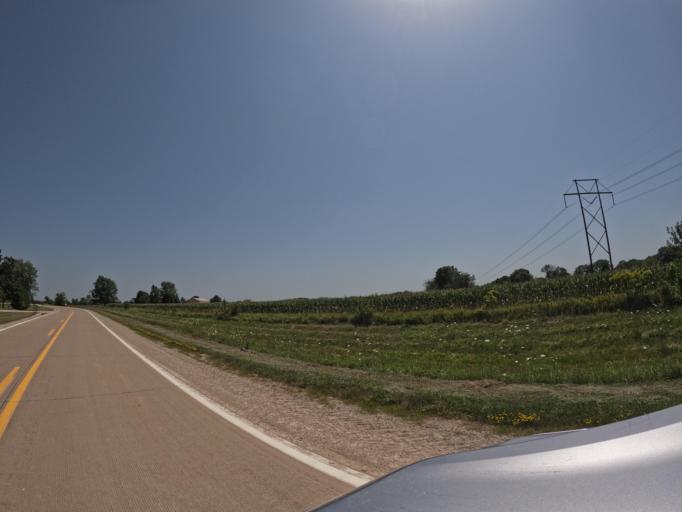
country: US
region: Iowa
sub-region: Henry County
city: Mount Pleasant
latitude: 40.9833
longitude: -91.6305
